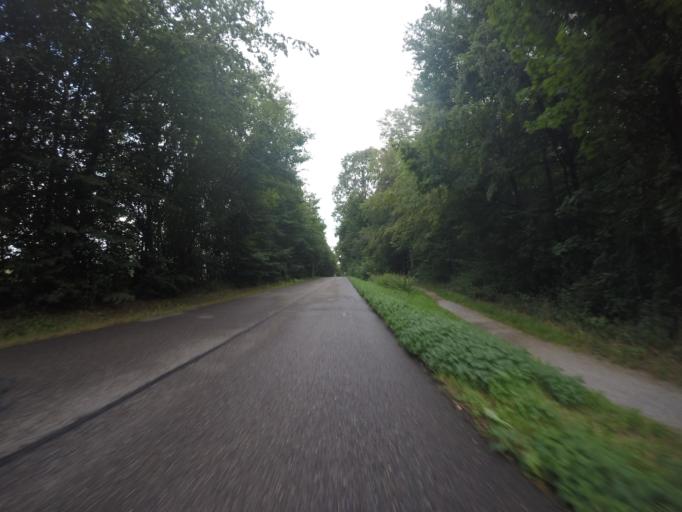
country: DE
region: Baden-Wuerttemberg
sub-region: Regierungsbezirk Stuttgart
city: Stuttgart-Ost
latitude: 48.7360
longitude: 9.1987
